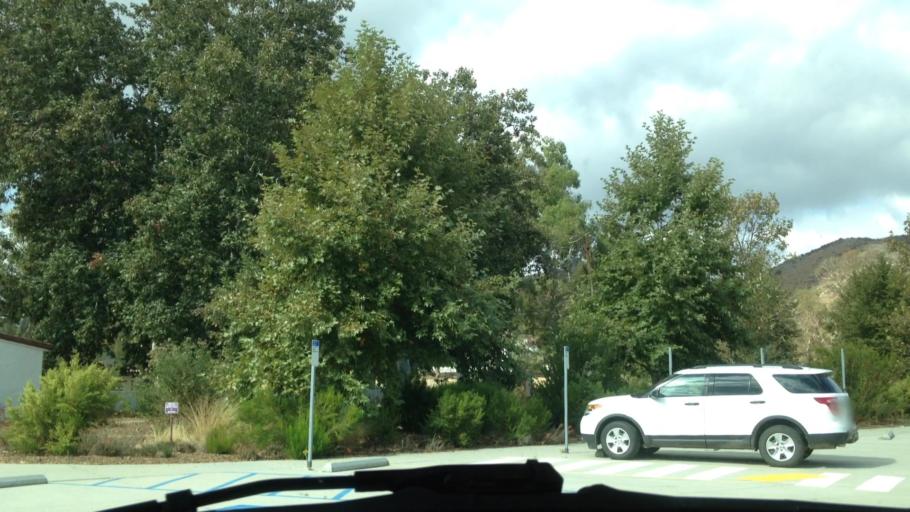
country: US
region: California
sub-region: Los Angeles County
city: Agoura
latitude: 34.1026
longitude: -118.7071
